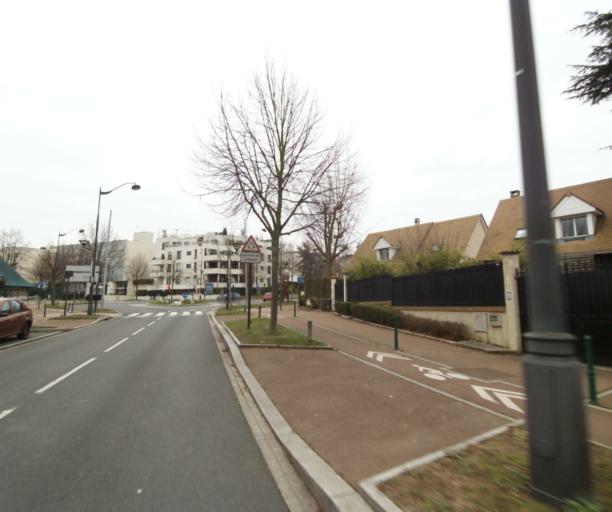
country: FR
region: Ile-de-France
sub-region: Departement des Hauts-de-Seine
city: Saint-Cloud
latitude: 48.8552
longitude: 2.1979
